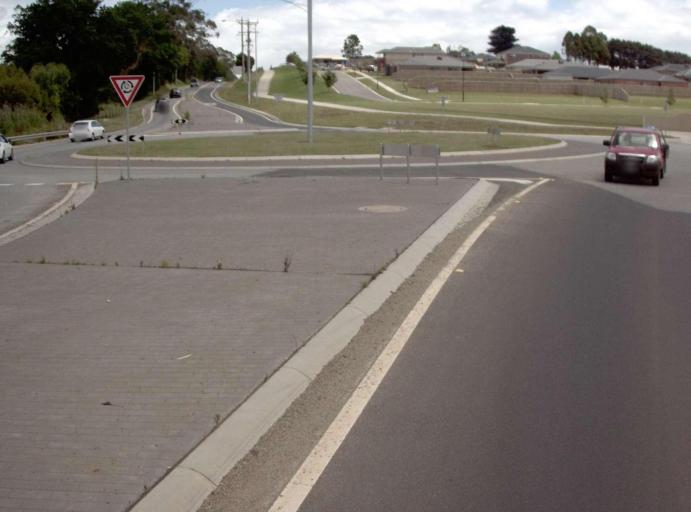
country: AU
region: Victoria
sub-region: Baw Baw
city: Warragul
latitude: -38.1499
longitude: 145.9054
